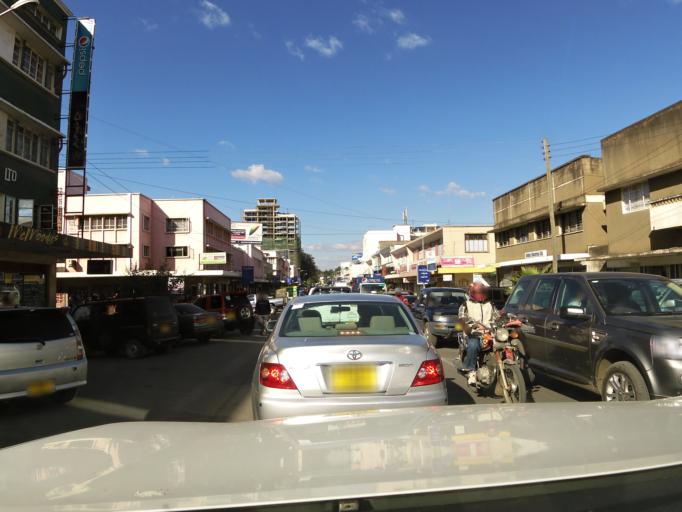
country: TZ
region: Arusha
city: Arusha
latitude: -3.3741
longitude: 36.6861
